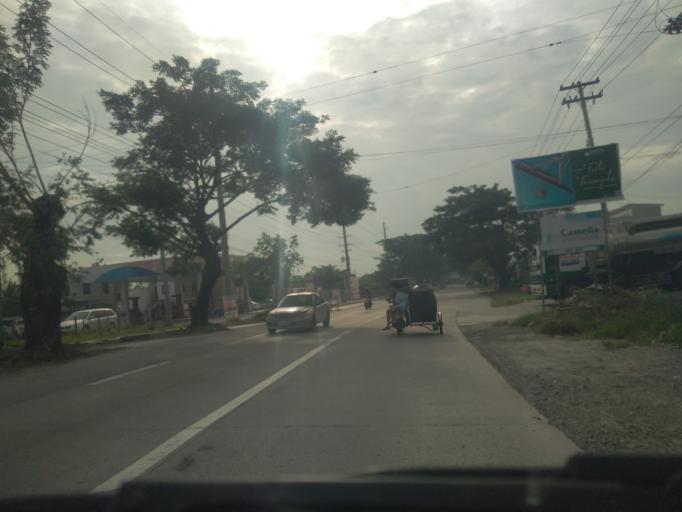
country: PH
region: Central Luzon
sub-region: Province of Pampanga
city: Calibutbut
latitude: 15.1254
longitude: 120.5853
